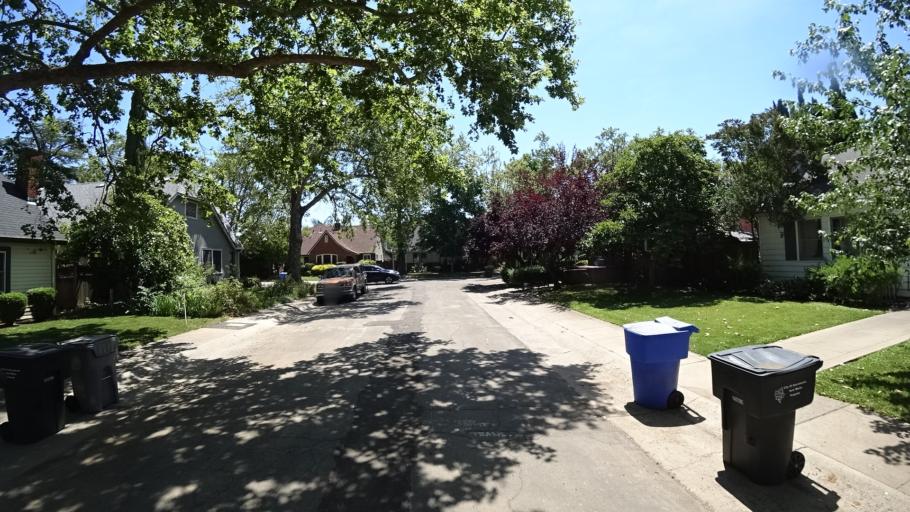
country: US
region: California
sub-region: Sacramento County
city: Sacramento
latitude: 38.5609
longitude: -121.4485
